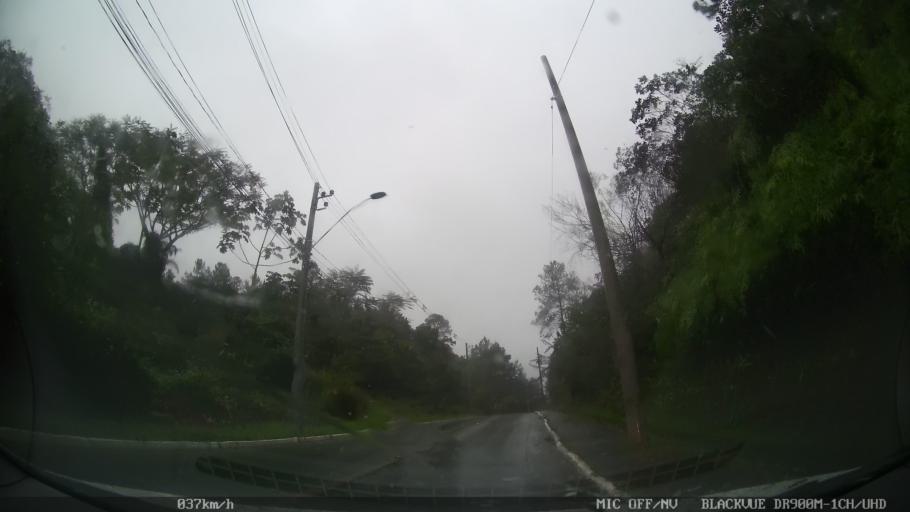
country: BR
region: Santa Catarina
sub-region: Itajai
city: Itajai
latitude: -26.9317
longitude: -48.6382
